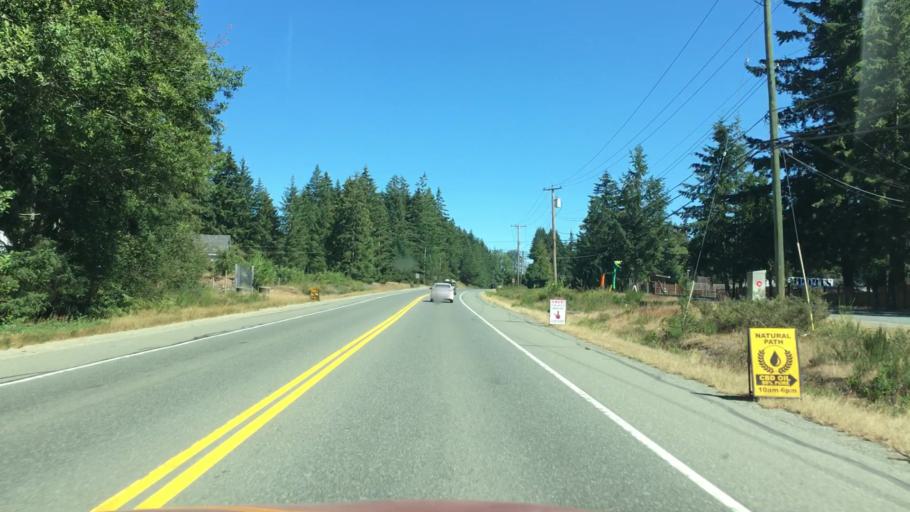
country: CA
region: British Columbia
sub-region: Regional District of Nanaimo
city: Parksville
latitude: 49.3117
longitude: -124.5055
